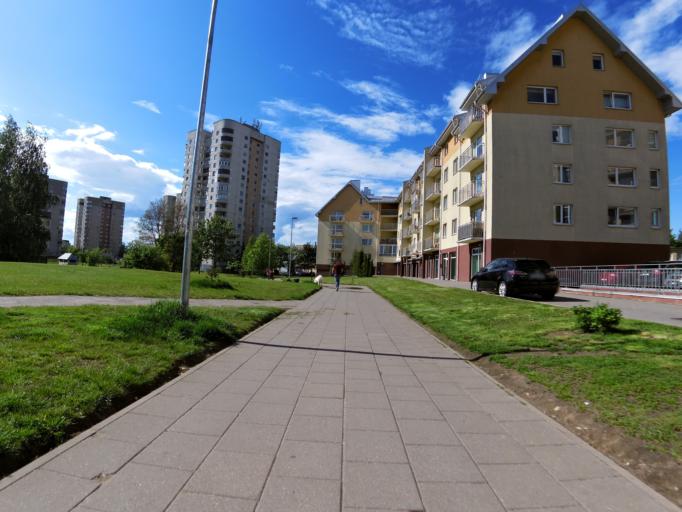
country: LT
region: Vilnius County
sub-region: Vilnius
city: Fabijoniskes
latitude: 54.7287
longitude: 25.2481
